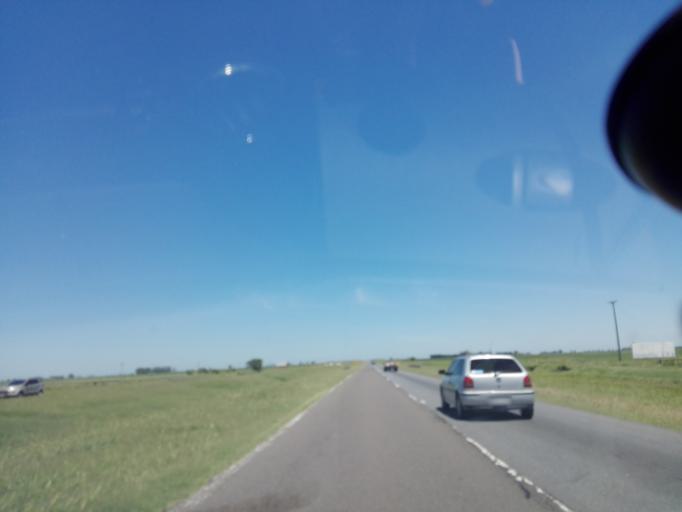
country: AR
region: Santa Fe
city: Carcarana
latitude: -32.8899
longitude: -61.0937
